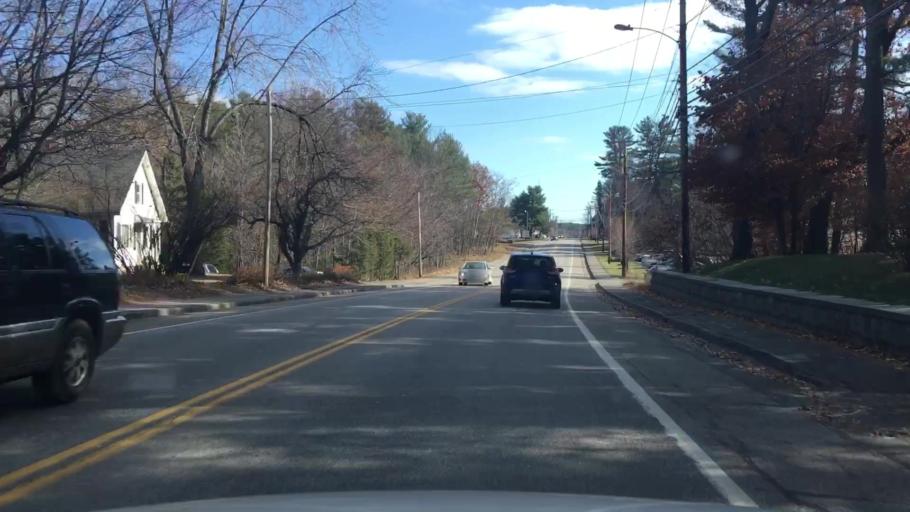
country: US
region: Maine
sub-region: Kennebec County
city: Augusta
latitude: 44.3080
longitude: -69.7543
